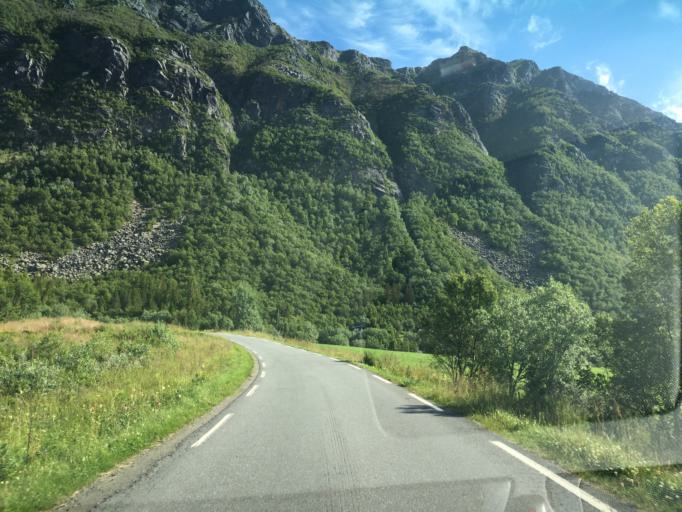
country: NO
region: Nordland
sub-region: Vagan
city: Svolvaer
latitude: 68.3986
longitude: 14.5791
